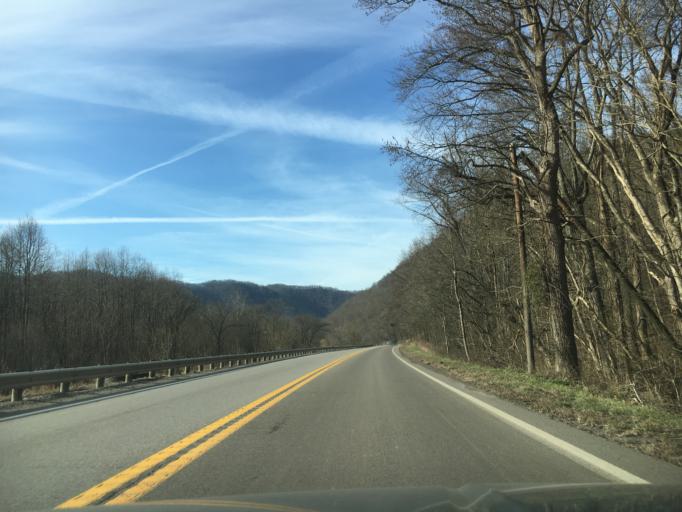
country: US
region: West Virginia
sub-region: Kanawha County
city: Montgomery
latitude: 38.1878
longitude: -81.3512
